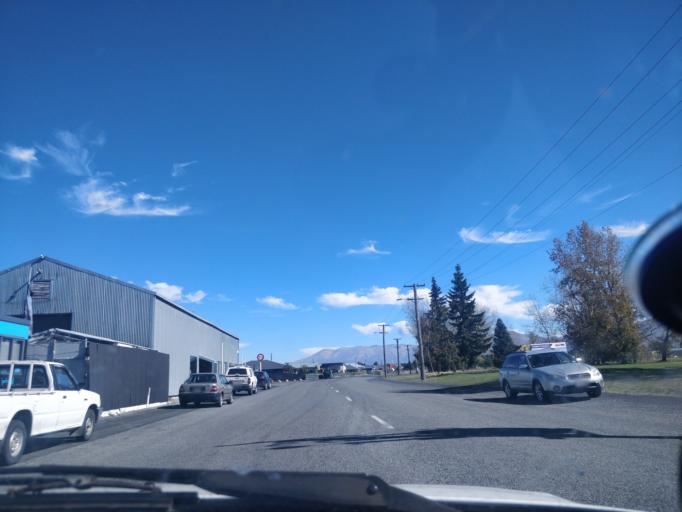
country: NZ
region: Canterbury
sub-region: Timaru District
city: Pleasant Point
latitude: -44.2639
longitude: 170.0987
